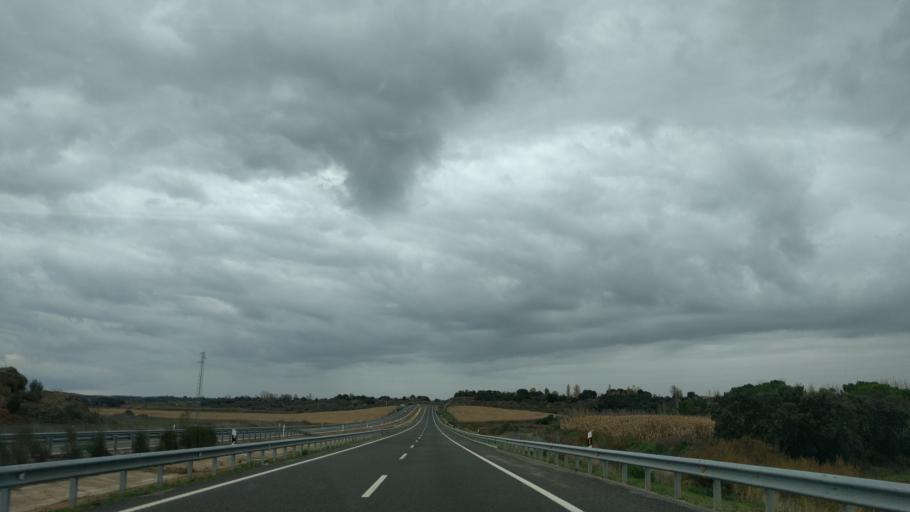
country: ES
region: Aragon
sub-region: Provincia de Huesca
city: Monzon
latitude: 41.9408
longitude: 0.1978
